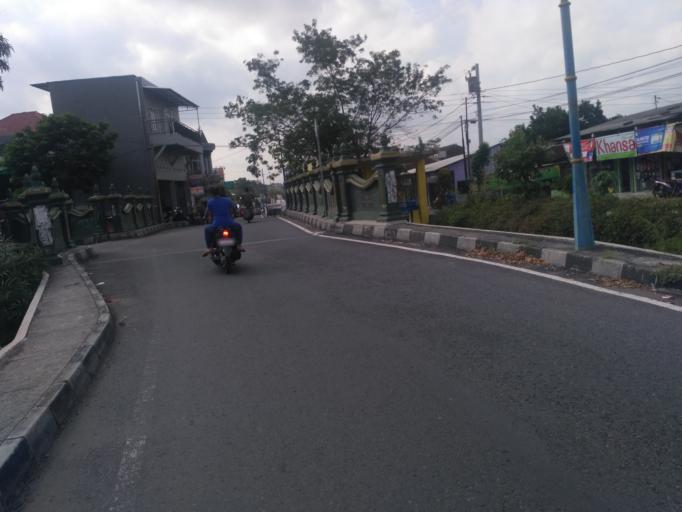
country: ID
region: Daerah Istimewa Yogyakarta
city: Yogyakarta
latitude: -7.7619
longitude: 110.3680
